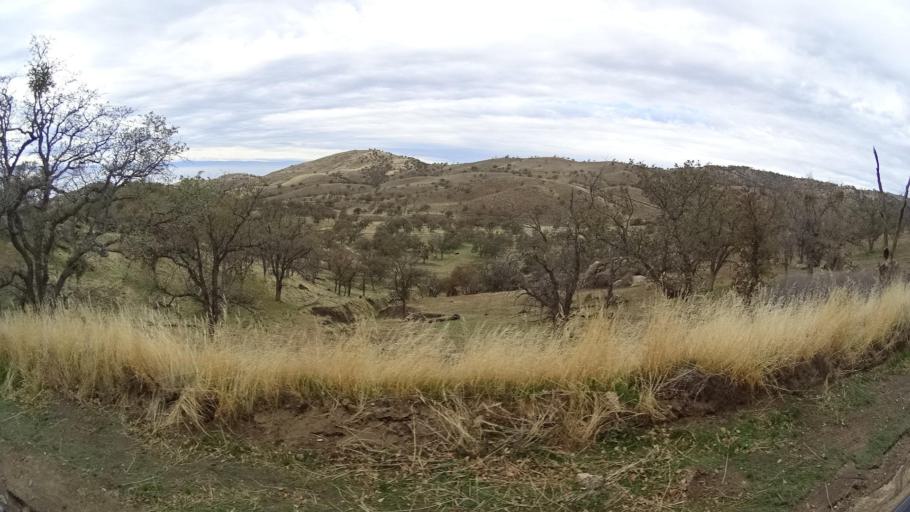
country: US
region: California
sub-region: Kern County
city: Stallion Springs
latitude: 35.1223
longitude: -118.7175
